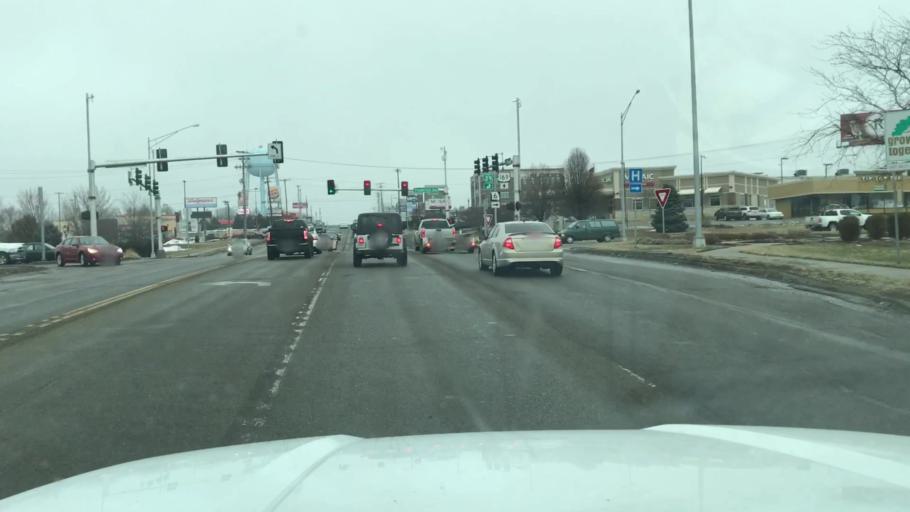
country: US
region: Missouri
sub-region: Buchanan County
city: Saint Joseph
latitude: 39.7764
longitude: -94.8032
